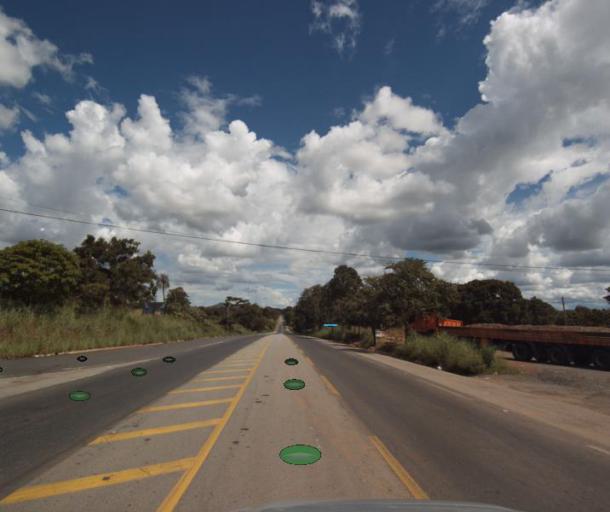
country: BR
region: Goias
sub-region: Porangatu
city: Porangatu
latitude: -13.7145
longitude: -49.0211
